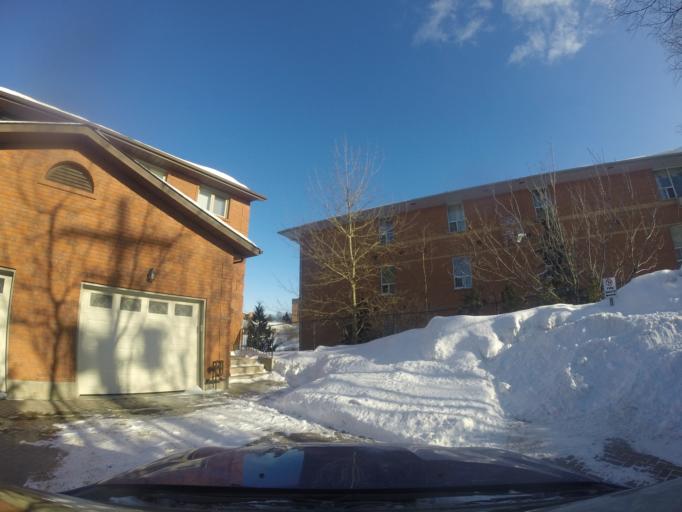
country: CA
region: Ontario
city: Greater Sudbury
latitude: 46.4541
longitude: -81.0011
